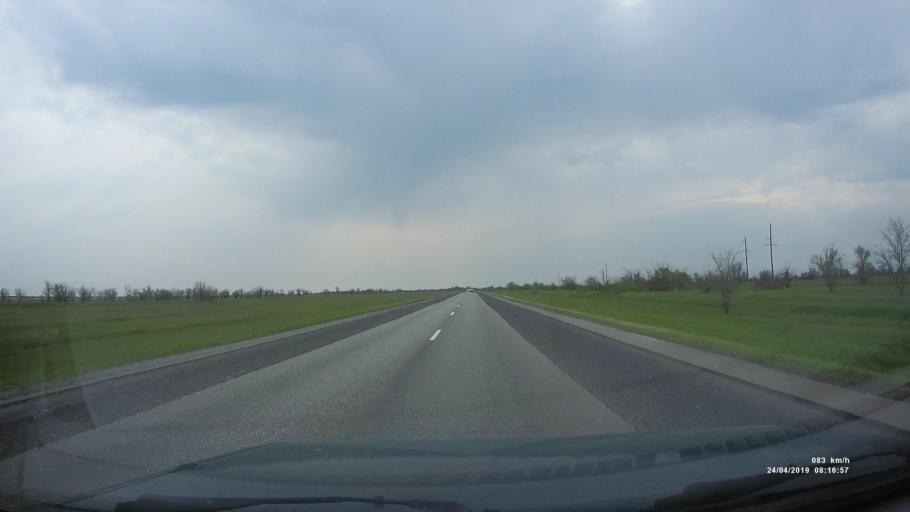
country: RU
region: Kalmykiya
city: Priyutnoye
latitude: 46.0984
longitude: 43.6212
